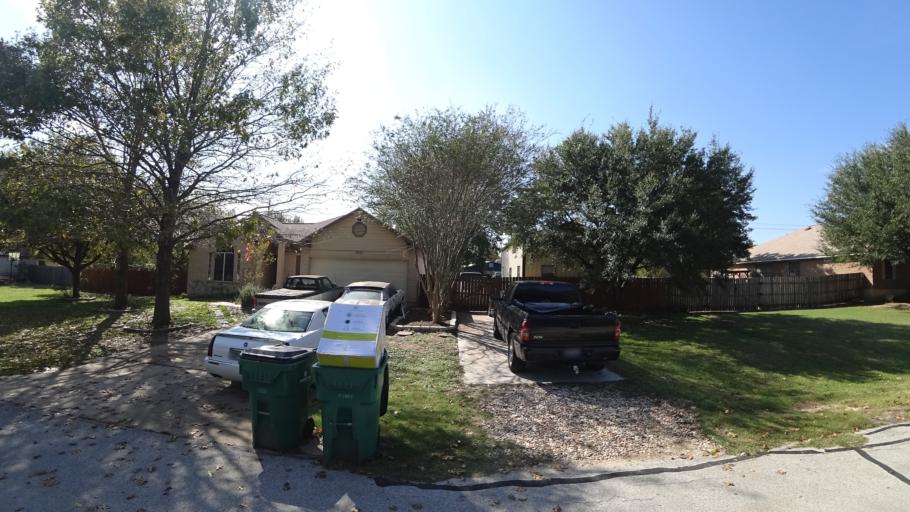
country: US
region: Texas
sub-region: Travis County
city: Pflugerville
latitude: 30.4252
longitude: -97.6317
